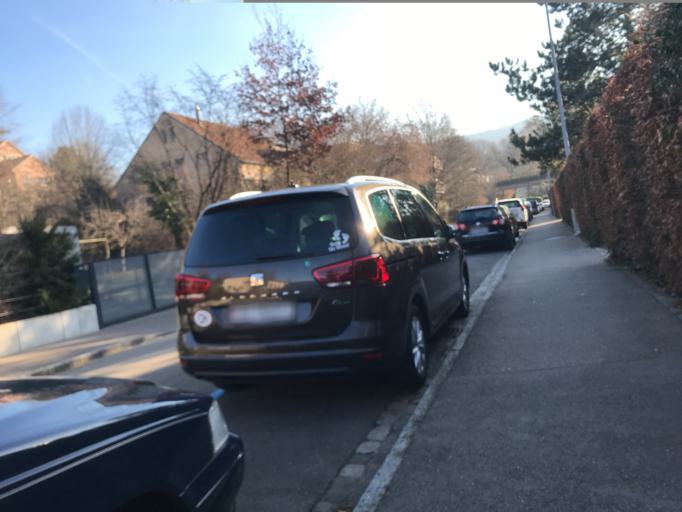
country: CH
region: Basel-City
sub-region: Basel-Stadt
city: Riehen
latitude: 47.5751
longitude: 7.6393
